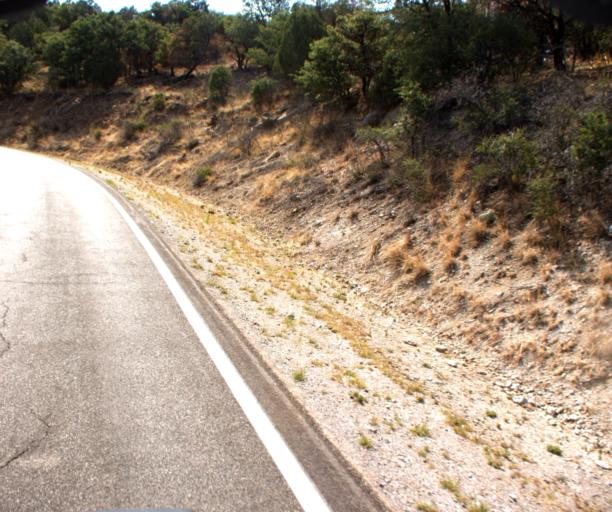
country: US
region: Arizona
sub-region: Greenlee County
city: Clifton
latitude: 33.0891
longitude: -109.0782
